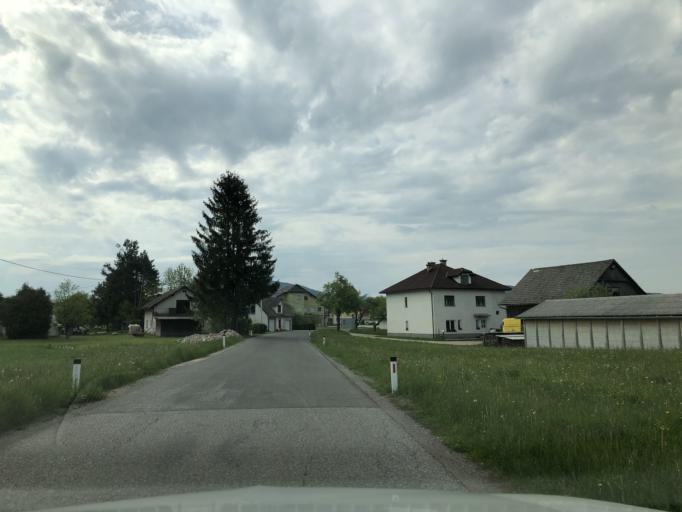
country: SI
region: Bloke
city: Nova Vas
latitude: 45.7754
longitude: 14.5053
